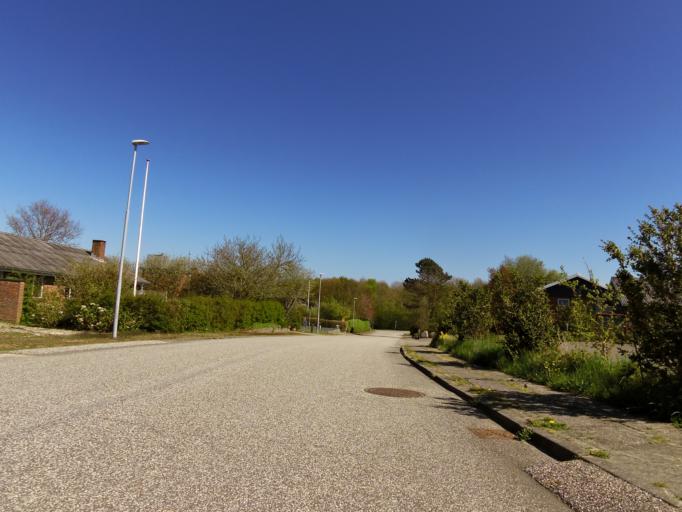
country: DK
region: Central Jutland
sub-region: Holstebro Kommune
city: Vinderup
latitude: 56.5943
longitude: 8.7853
